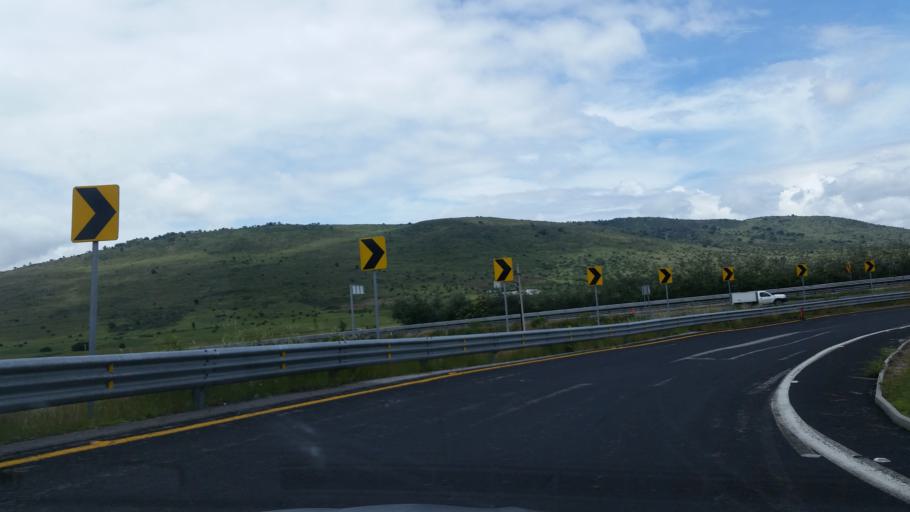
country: MX
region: Mexico
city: San Francisco Soyaniquilpan
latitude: 19.9982
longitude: -99.4919
